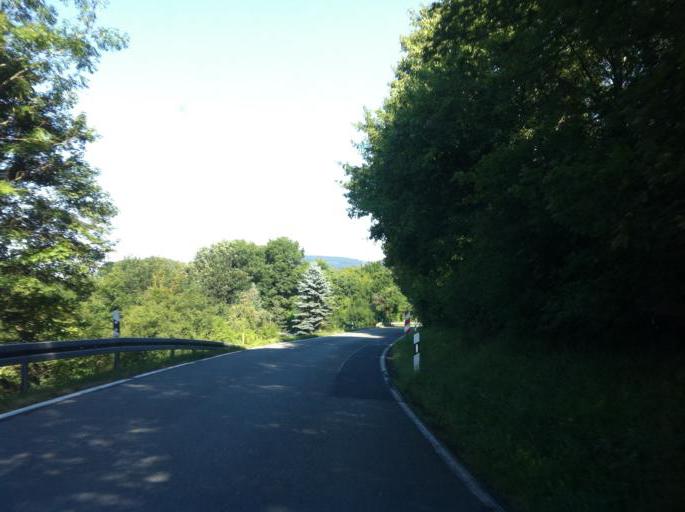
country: DE
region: Thuringia
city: Schalkau
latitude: 50.4154
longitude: 11.0410
